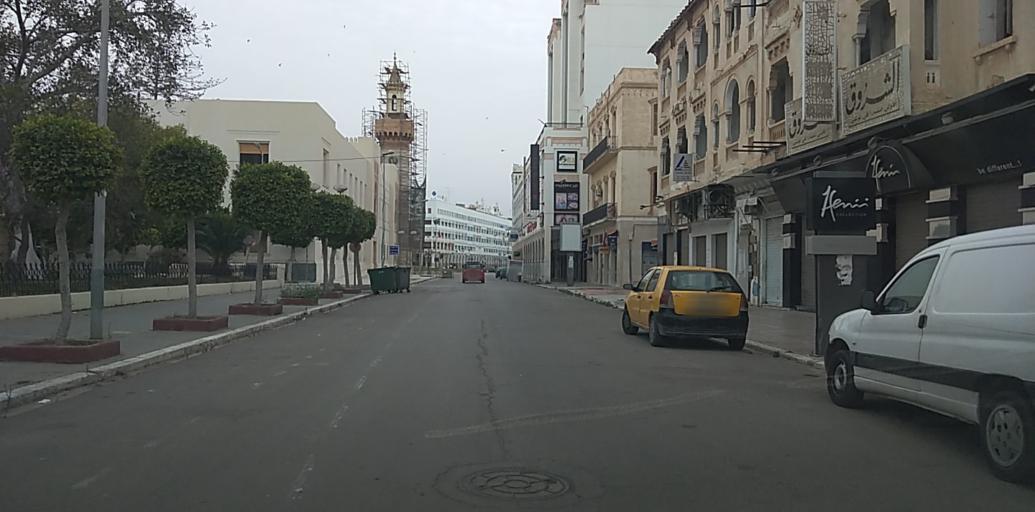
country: TN
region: Safaqis
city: Sfax
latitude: 34.7317
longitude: 10.7650
